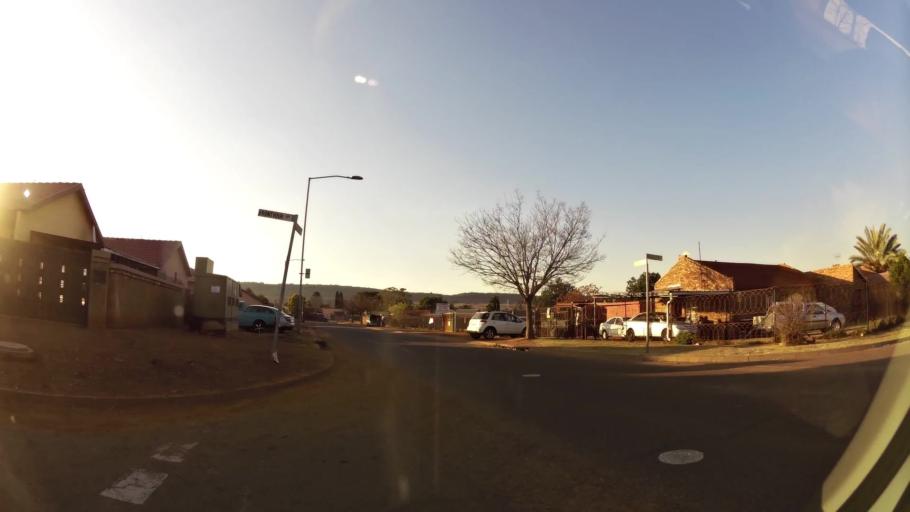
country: ZA
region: Gauteng
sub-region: City of Tshwane Metropolitan Municipality
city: Pretoria
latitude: -25.7438
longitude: 28.1097
